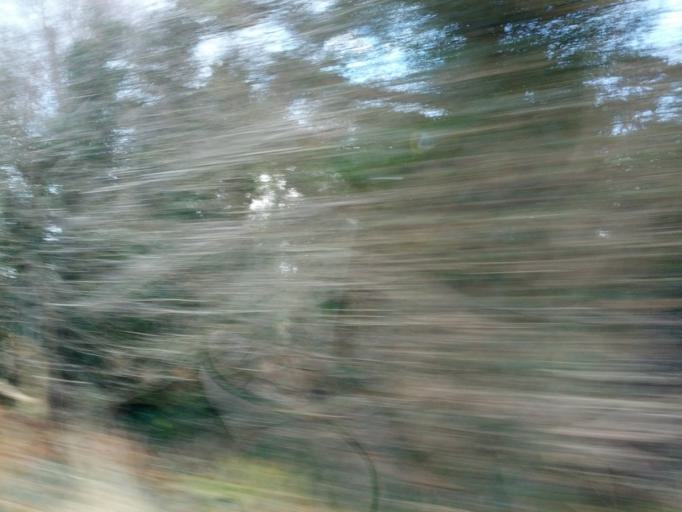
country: IE
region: Connaught
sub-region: County Galway
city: Athenry
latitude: 53.3598
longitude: -8.6693
